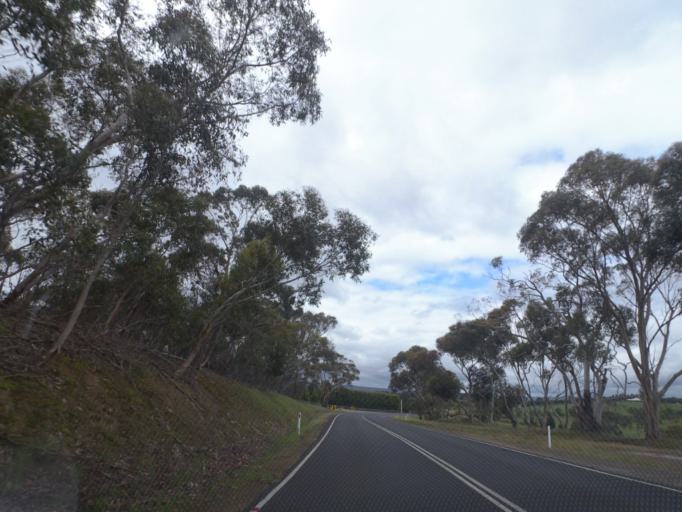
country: AU
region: Victoria
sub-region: Whittlesea
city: Whittlesea
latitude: -37.4971
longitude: 145.0895
